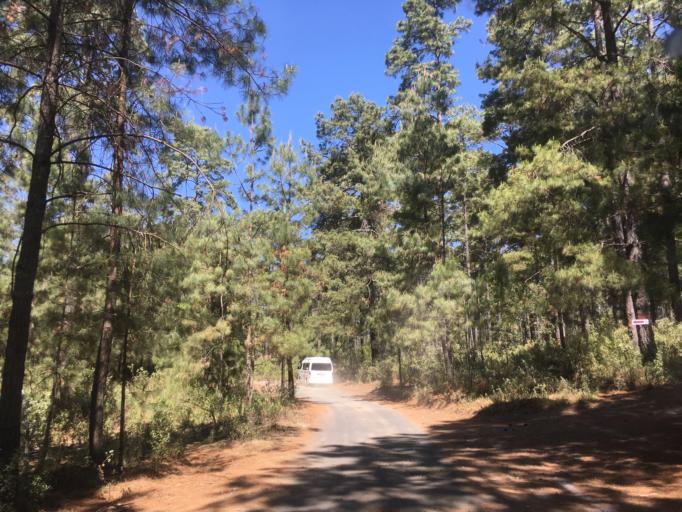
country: MX
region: Michoacan
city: Nuevo San Juan Parangaricutiro
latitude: 19.4593
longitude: -102.2068
